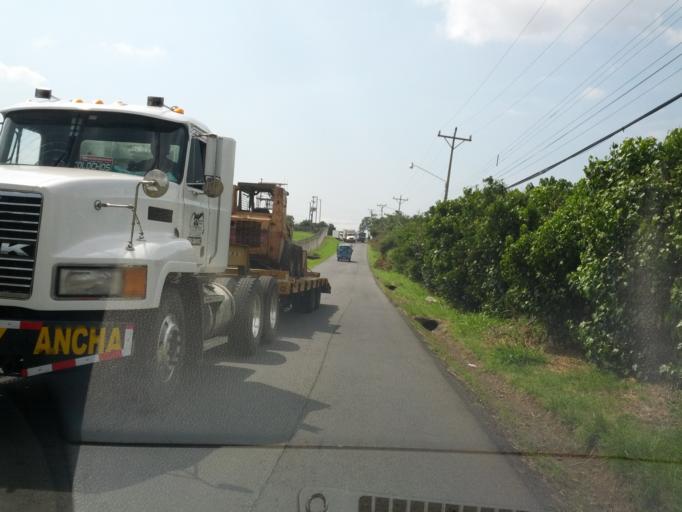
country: CR
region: Alajuela
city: Alajuela
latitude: 9.9912
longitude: -84.2222
